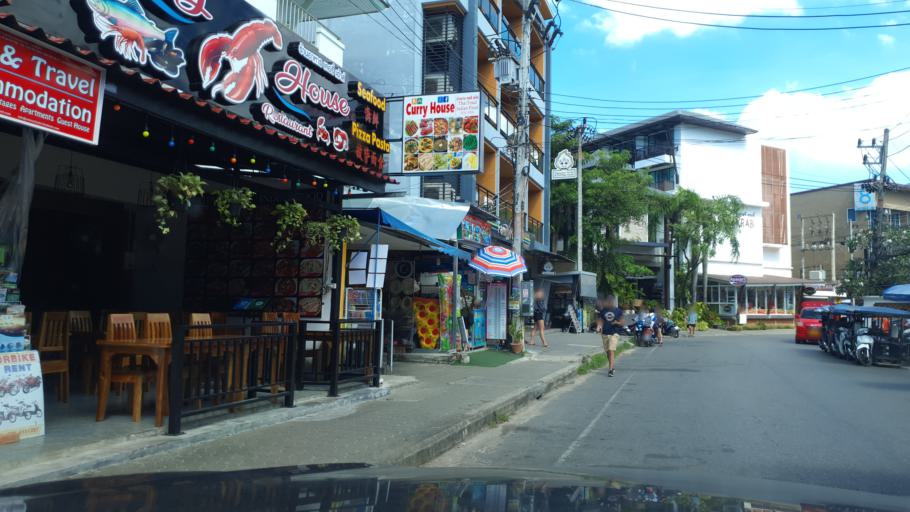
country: TH
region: Phangnga
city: Ban Ao Nang
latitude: 8.0402
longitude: 98.8175
